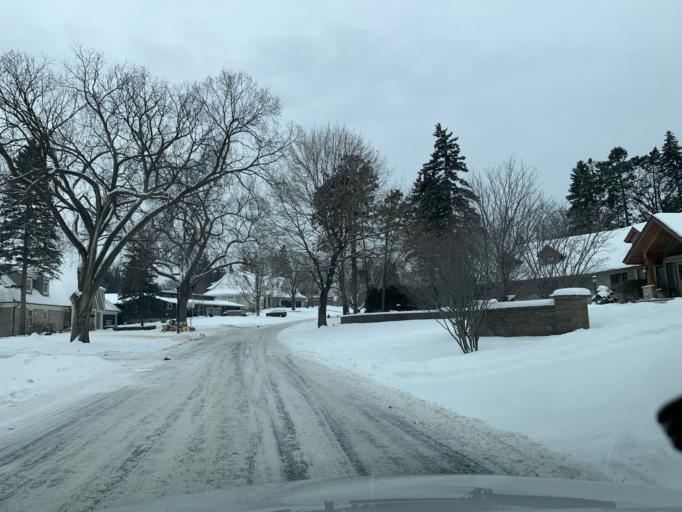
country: US
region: Minnesota
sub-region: Hennepin County
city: Edina
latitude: 44.9167
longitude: -93.3473
